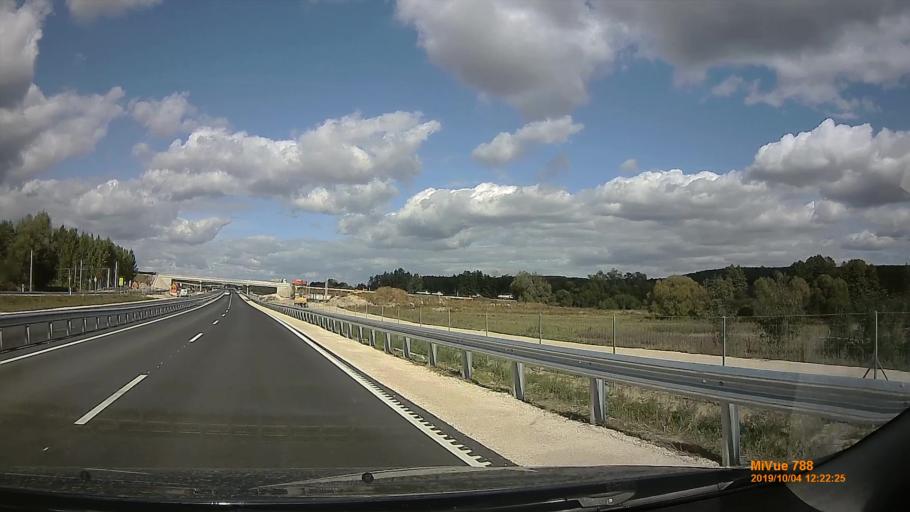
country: HU
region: Somogy
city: Karad
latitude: 46.6211
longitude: 17.7961
